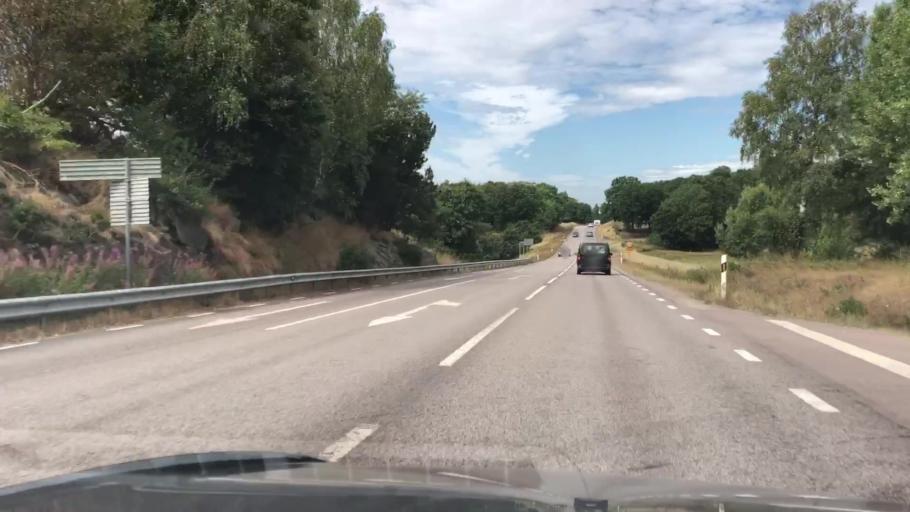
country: SE
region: Blekinge
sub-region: Karlskrona Kommun
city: Sturko
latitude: 56.1893
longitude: 15.7086
